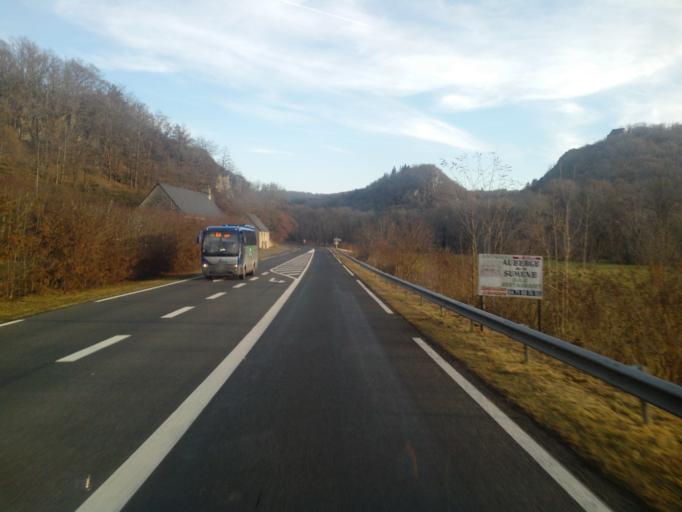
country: FR
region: Limousin
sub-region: Departement de la Correze
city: Bort-les-Orgues
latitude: 45.3438
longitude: 2.5293
